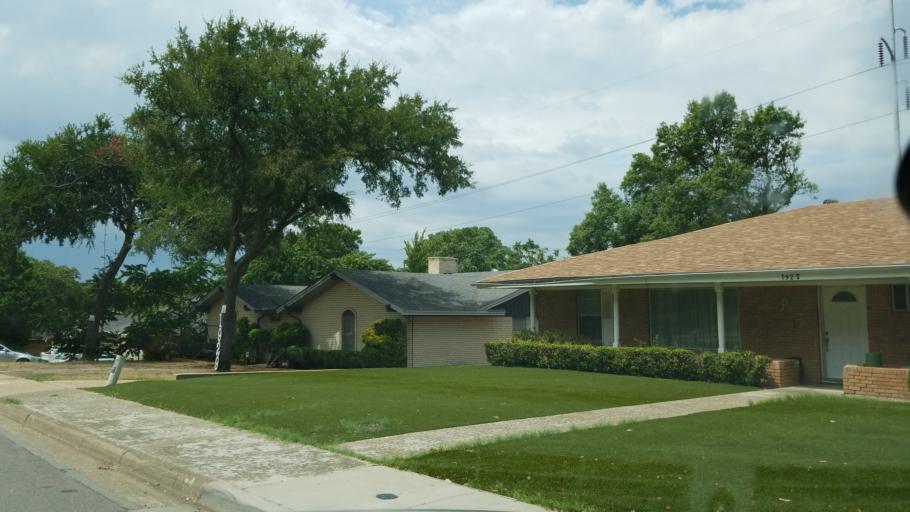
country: US
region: Texas
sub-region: Dallas County
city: Duncanville
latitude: 32.6615
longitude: -96.8517
